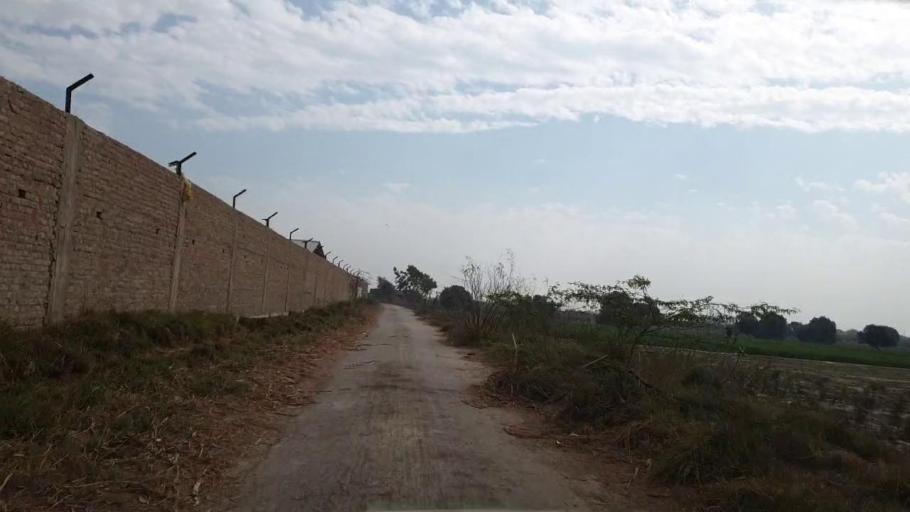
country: PK
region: Sindh
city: Matiari
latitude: 25.5798
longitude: 68.4414
